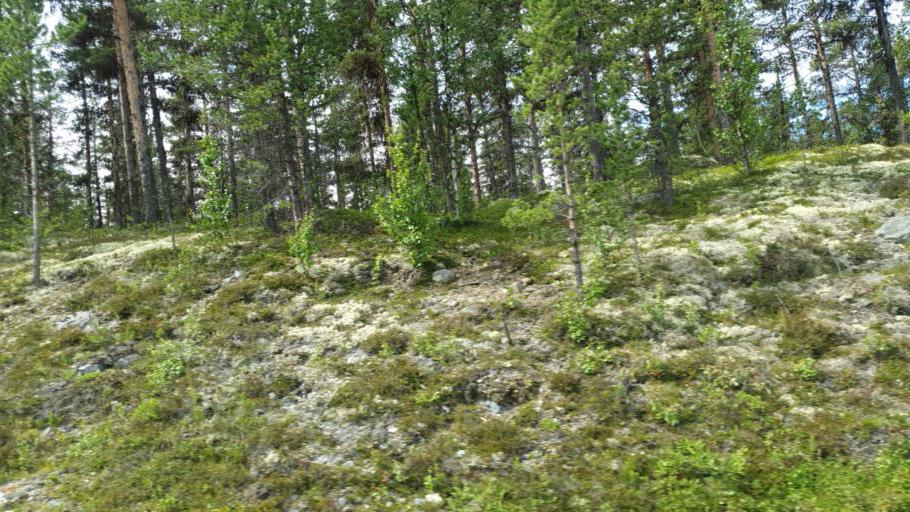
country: NO
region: Oppland
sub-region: Vaga
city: Vagamo
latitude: 61.7089
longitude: 9.0571
